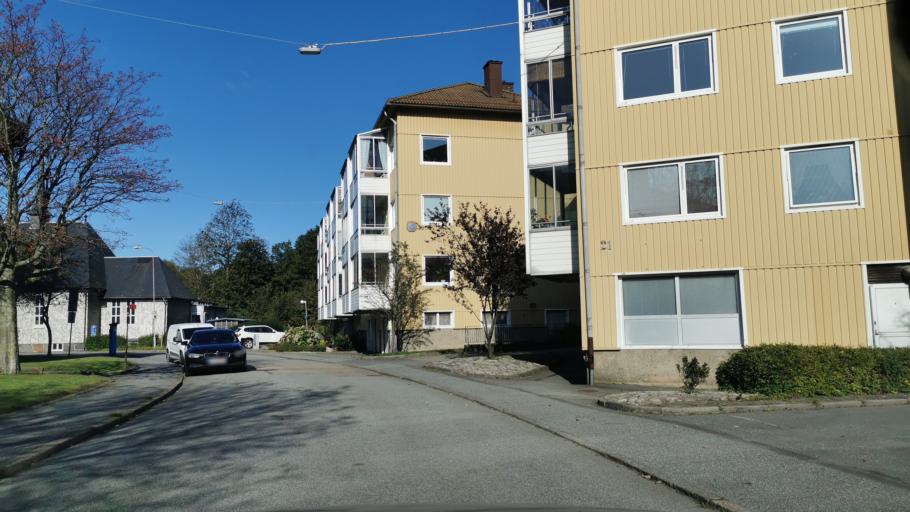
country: SE
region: Vaestra Goetaland
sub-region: Goteborg
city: Eriksbo
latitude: 57.7352
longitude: 12.0080
